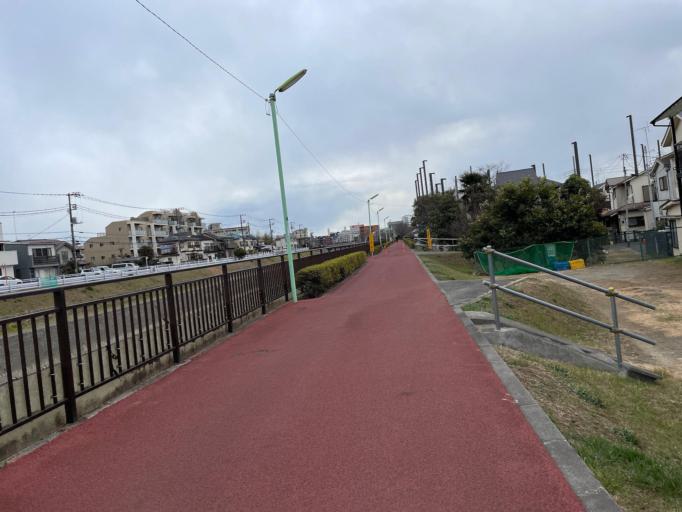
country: JP
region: Tokyo
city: Chofugaoka
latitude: 35.6190
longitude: 139.6141
